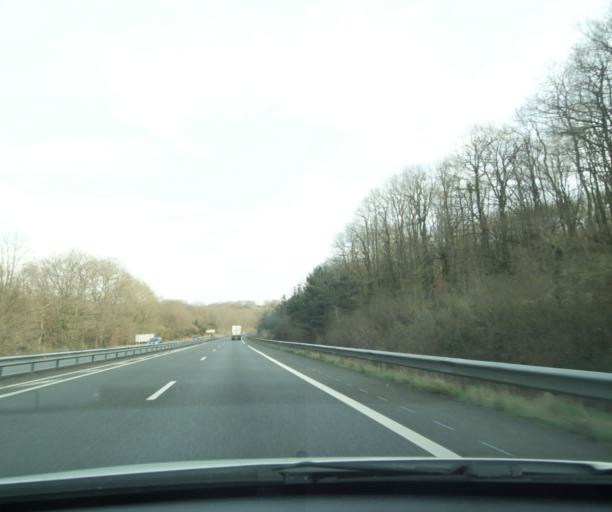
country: FR
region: Midi-Pyrenees
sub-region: Departement des Hautes-Pyrenees
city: Barbazan-Debat
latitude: 43.2082
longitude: 0.1380
